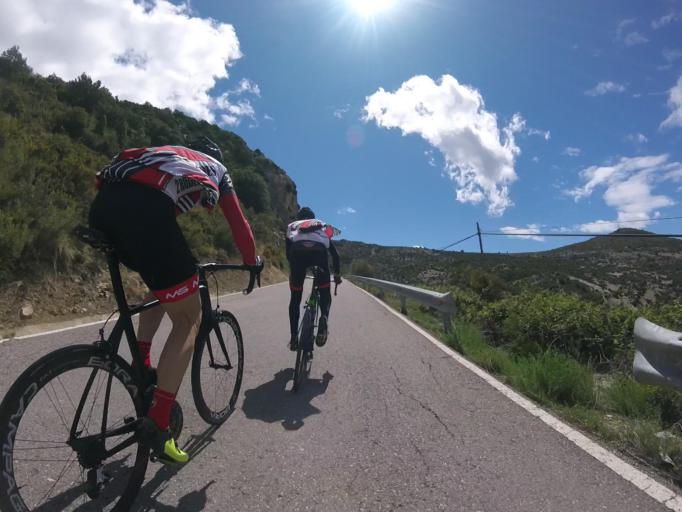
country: ES
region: Valencia
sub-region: Provincia de Castello
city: Sierra-Engarceran
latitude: 40.2848
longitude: -0.0357
